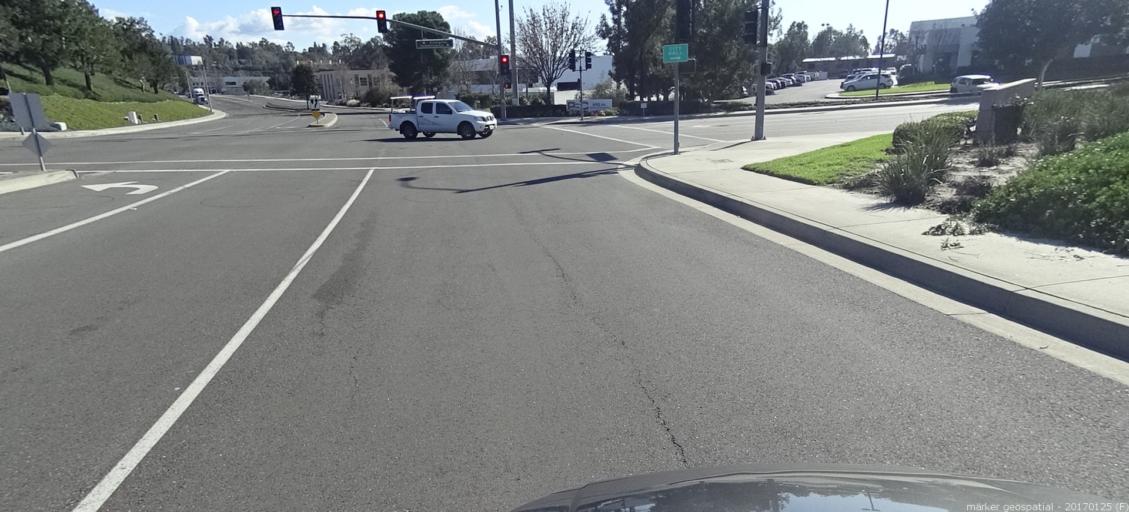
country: US
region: California
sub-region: Orange County
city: Lake Forest
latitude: 33.6650
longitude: -117.6754
